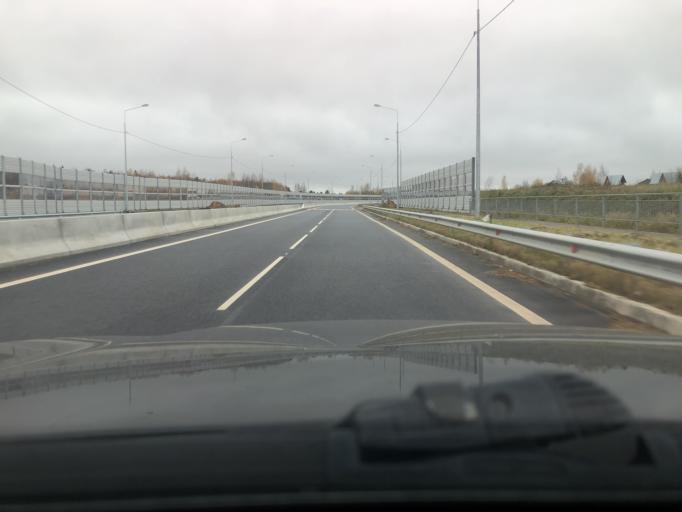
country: RU
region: Moskovskaya
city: Semkhoz
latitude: 56.3192
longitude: 38.0824
